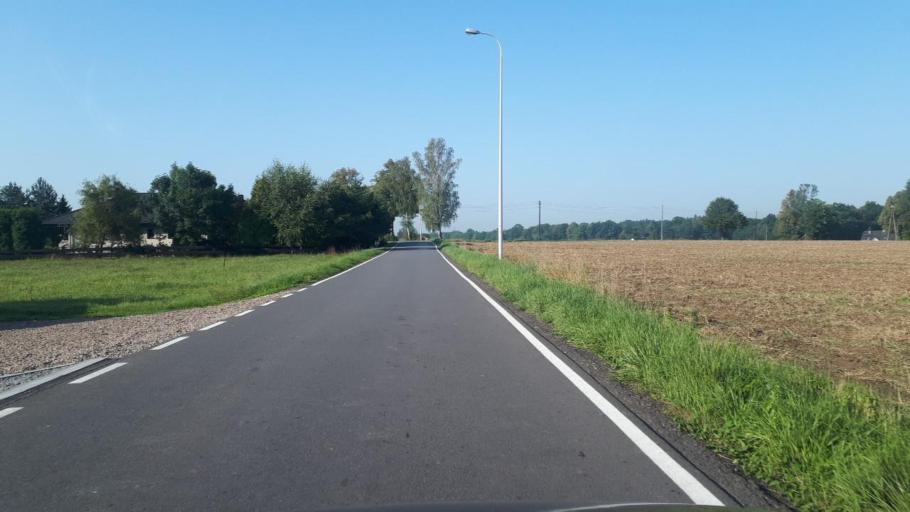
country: PL
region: Silesian Voivodeship
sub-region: Powiat cieszynski
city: Piersciec
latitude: 49.8480
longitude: 18.8336
